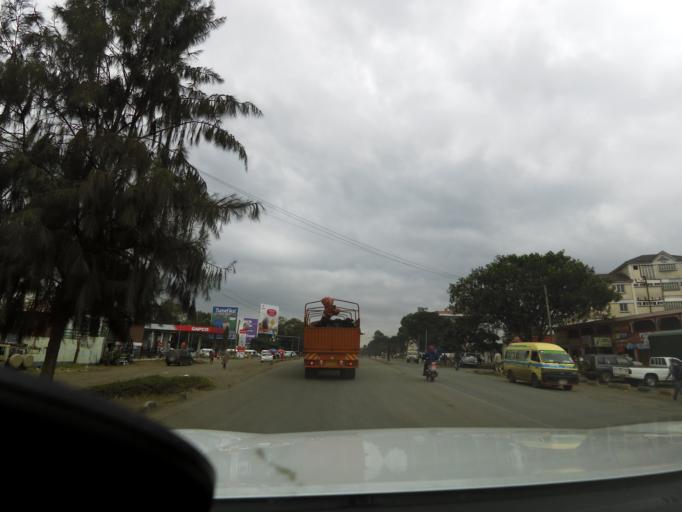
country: TZ
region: Arusha
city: Arusha
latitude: -3.3619
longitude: 36.6845
